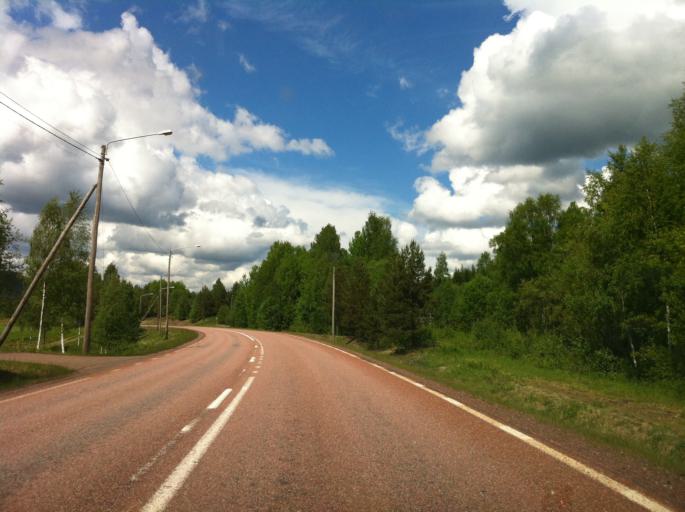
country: SE
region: Dalarna
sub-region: Malung-Saelens kommun
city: Malung
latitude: 60.9518
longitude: 13.3530
